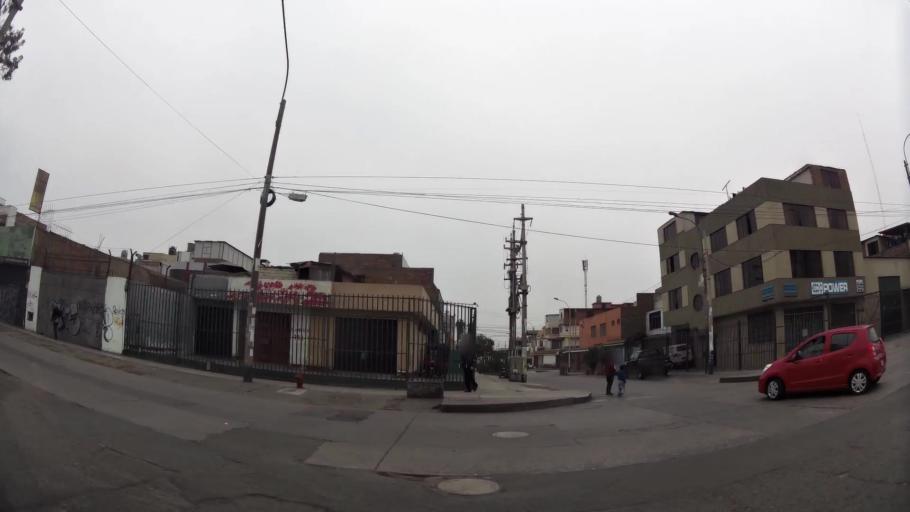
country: PE
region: Lima
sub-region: Lima
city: San Luis
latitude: -12.0817
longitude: -77.0134
